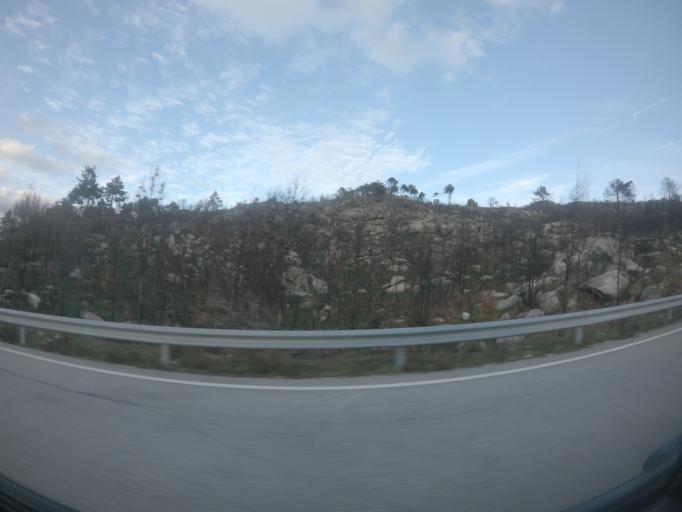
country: PT
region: Braganca
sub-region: Carrazeda de Ansiaes
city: Carrazeda de Anciaes
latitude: 41.2569
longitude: -7.3183
